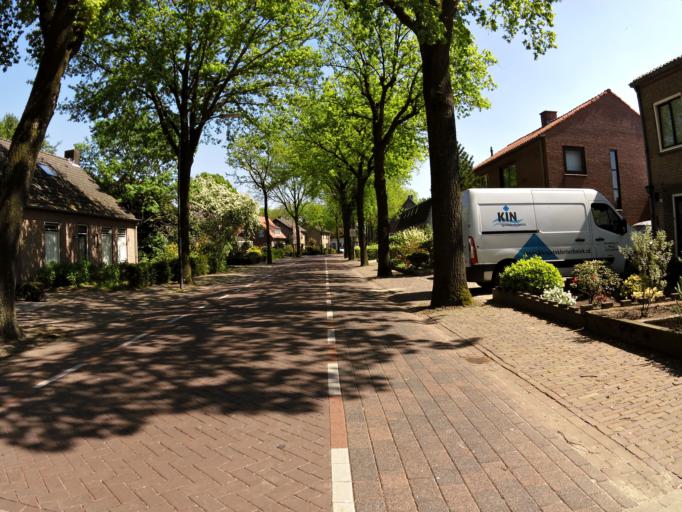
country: NL
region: North Brabant
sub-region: Gemeente Vught
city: Vught
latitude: 51.6596
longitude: 5.2354
